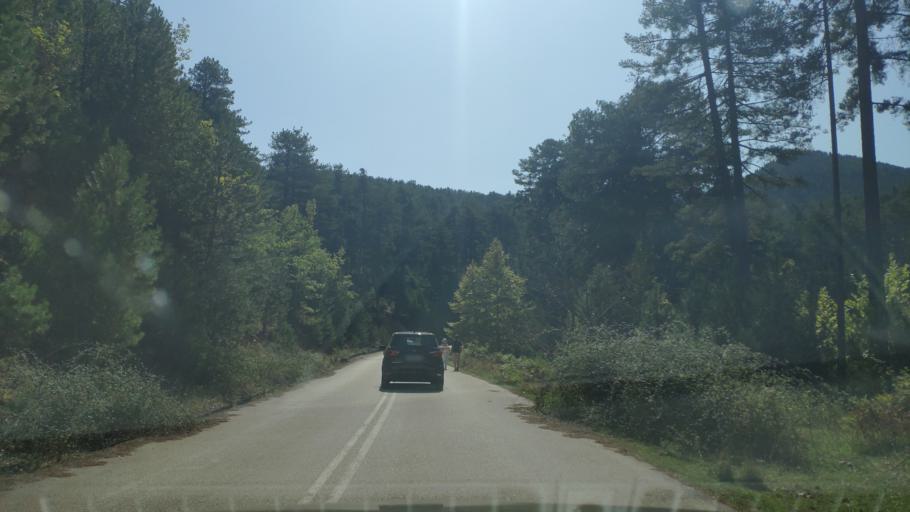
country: GR
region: West Greece
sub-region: Nomos Achaias
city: Kalavryta
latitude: 37.9267
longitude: 22.2861
